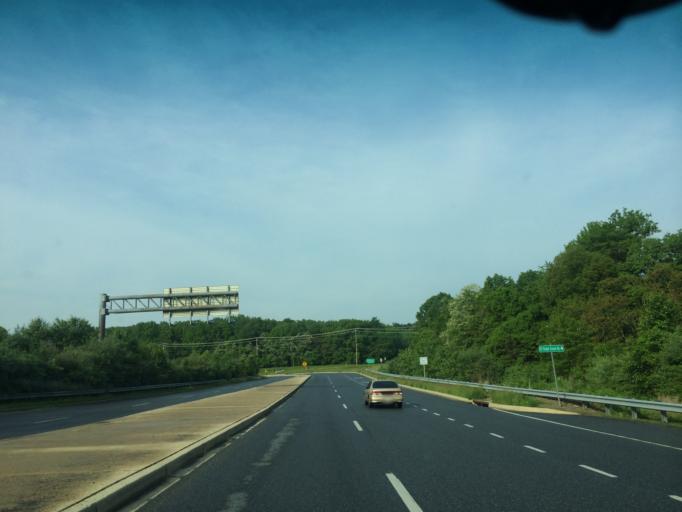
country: US
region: Maryland
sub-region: Howard County
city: Riverside
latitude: 39.1832
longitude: -76.8977
